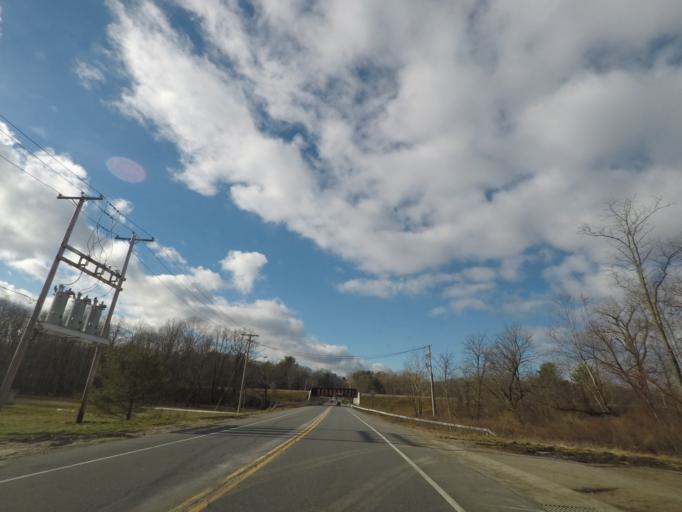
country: US
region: New York
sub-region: Schenectady County
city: East Glenville
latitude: 42.8672
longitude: -73.9011
